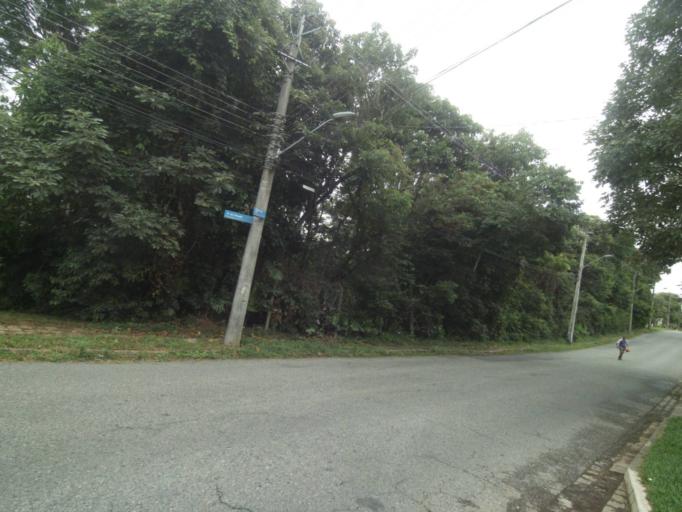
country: BR
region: Parana
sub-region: Curitiba
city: Curitiba
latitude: -25.4117
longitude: -49.2880
